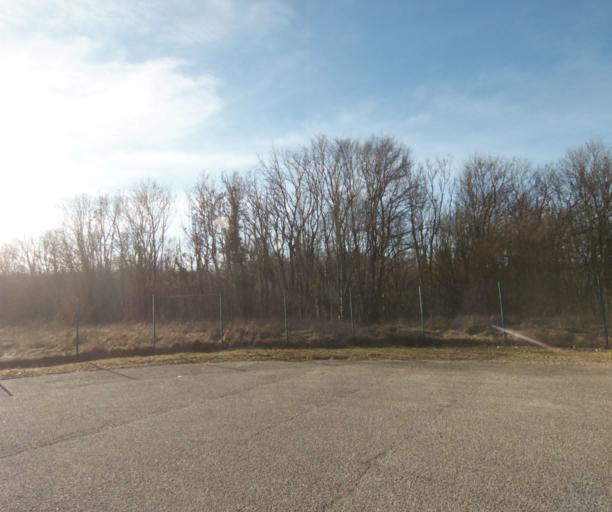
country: FR
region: Lorraine
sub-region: Departement de Meurthe-et-Moselle
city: Villers-les-Nancy
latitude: 48.6560
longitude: 6.1289
